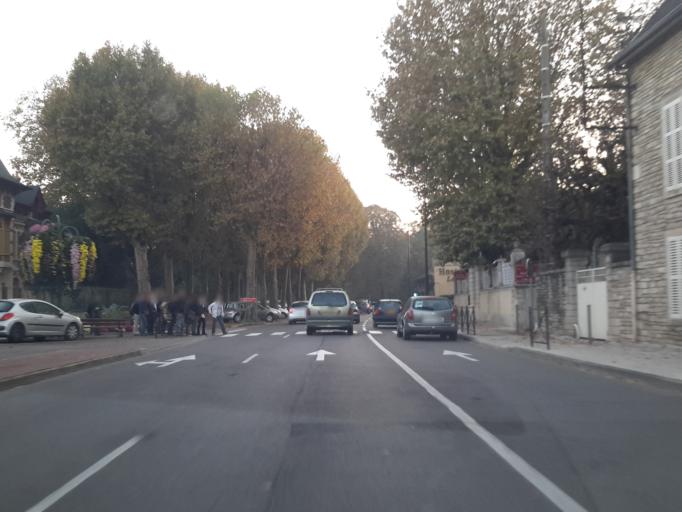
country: FR
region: Bourgogne
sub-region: Departement de la Cote-d'Or
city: Beaune
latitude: 47.0275
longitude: 4.8365
